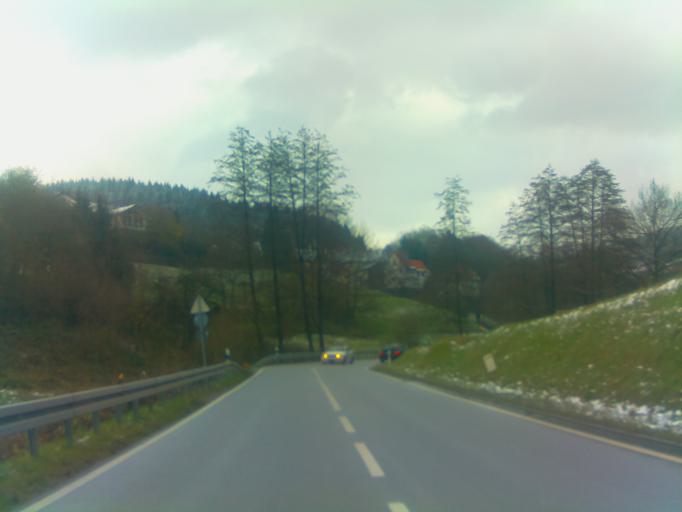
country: DE
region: Hesse
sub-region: Regierungsbezirk Darmstadt
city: Wald-Michelbach
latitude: 49.5707
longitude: 8.7950
